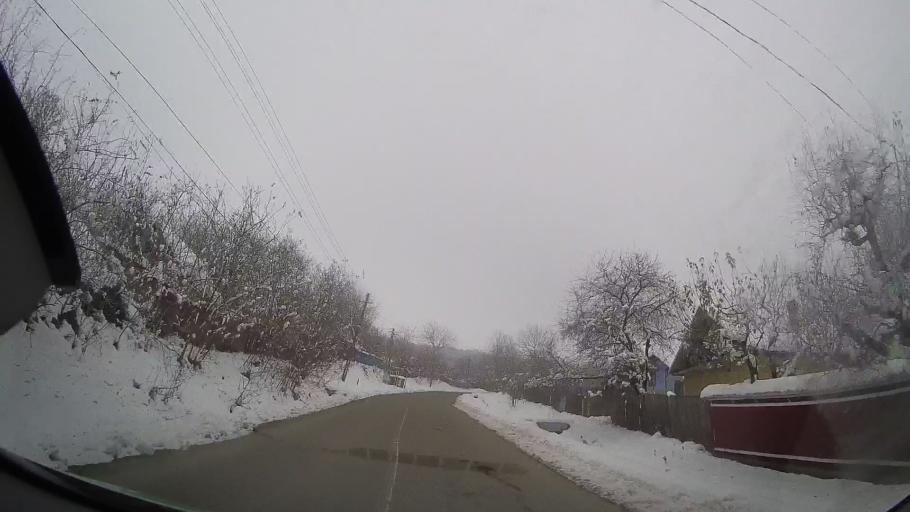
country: RO
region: Neamt
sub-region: Comuna Bozieni
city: Bozieni
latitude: 46.8517
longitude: 27.1798
